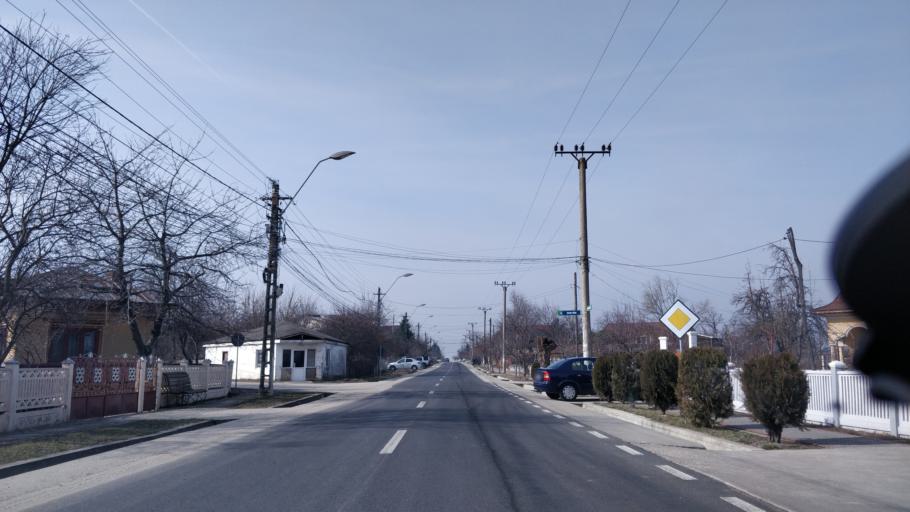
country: RO
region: Giurgiu
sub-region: Comuna Bolintin Deal
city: Bolintin Deal
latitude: 44.4609
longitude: 25.8092
